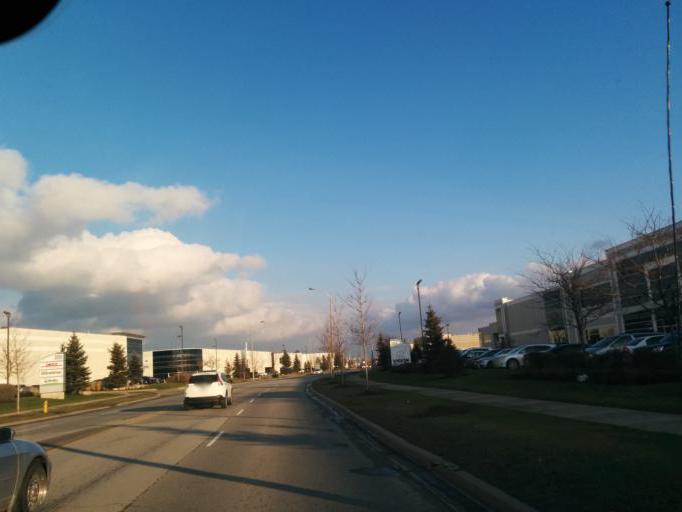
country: CA
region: Ontario
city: Etobicoke
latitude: 43.7766
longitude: -79.6317
